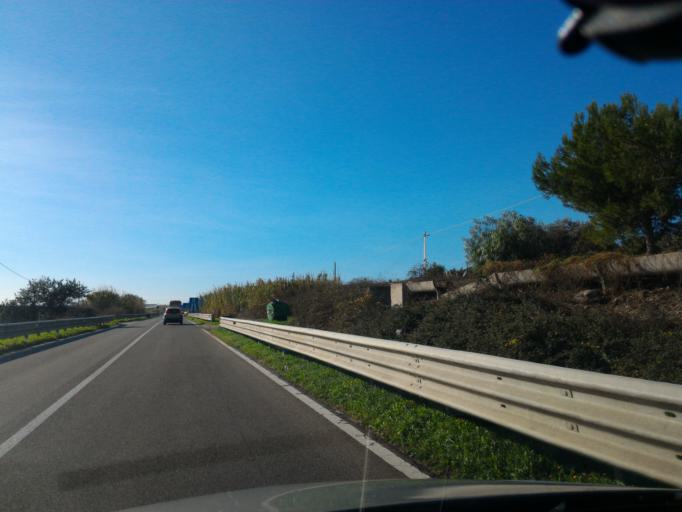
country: IT
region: Calabria
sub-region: Provincia di Crotone
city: Tronca
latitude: 39.1696
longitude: 17.1014
